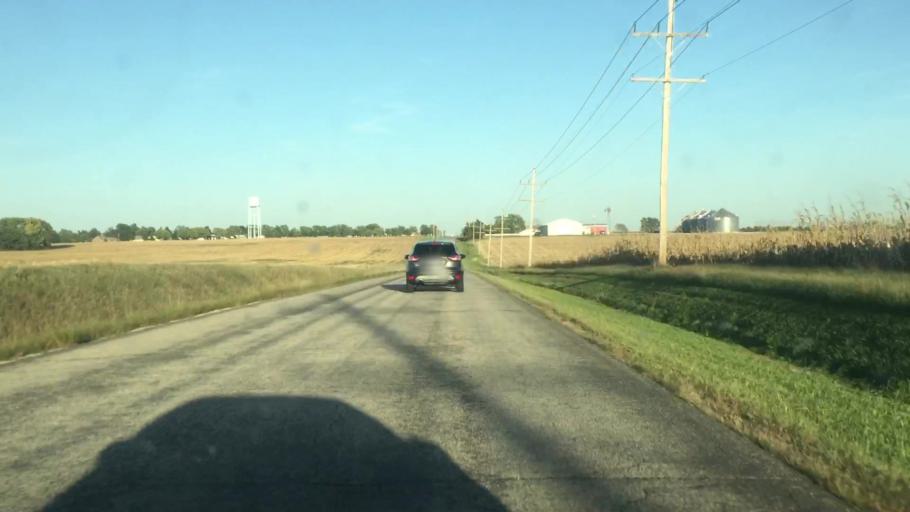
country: US
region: Kansas
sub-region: Atchison County
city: Atchison
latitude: 39.5656
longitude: -95.3170
